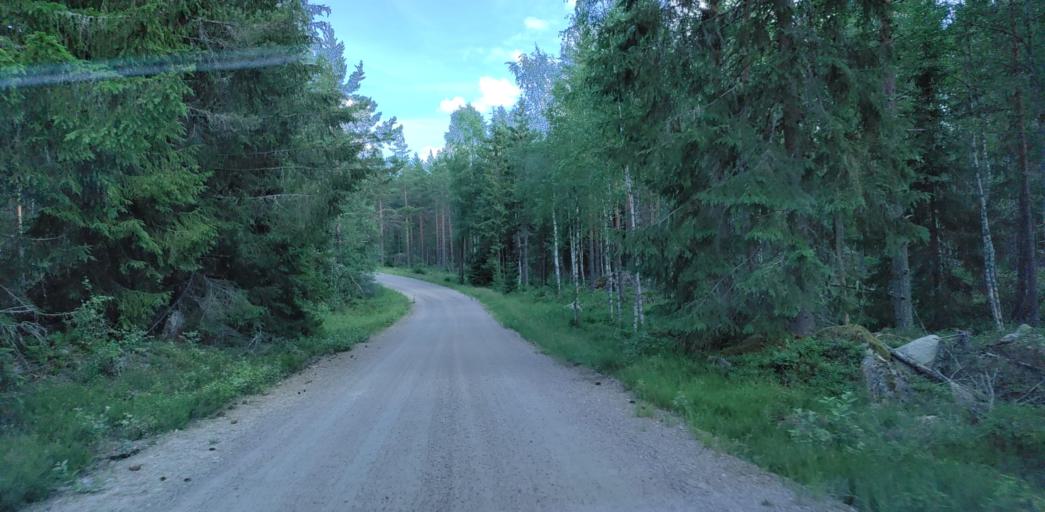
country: SE
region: Vaermland
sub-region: Hagfors Kommun
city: Ekshaerad
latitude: 60.0931
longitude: 13.4151
